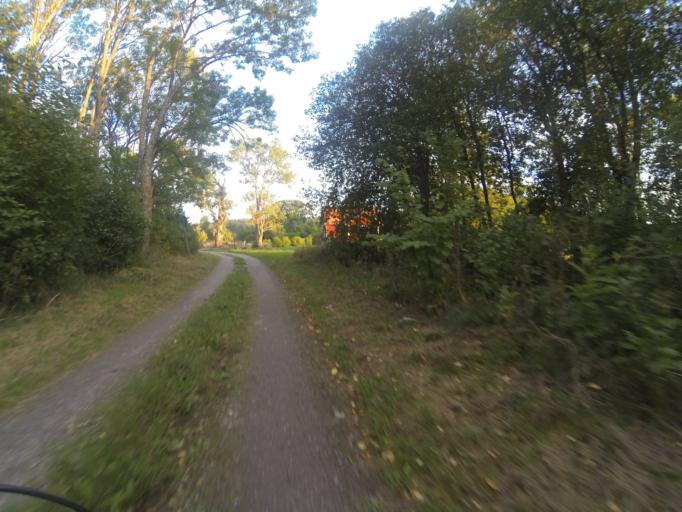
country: SE
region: Soedermanland
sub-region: Eskilstuna Kommun
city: Hallbybrunn
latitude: 59.4451
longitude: 16.3908
